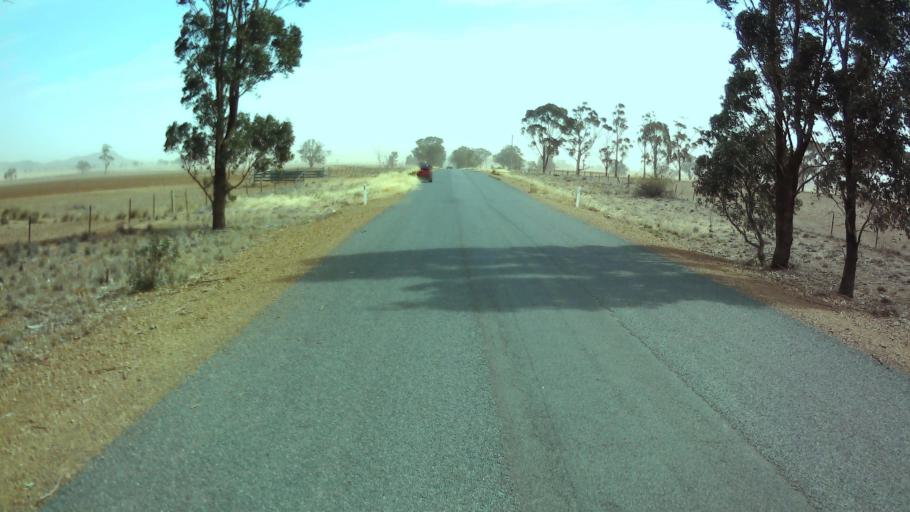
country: AU
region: New South Wales
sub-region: Weddin
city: Grenfell
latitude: -33.7663
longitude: 147.9877
